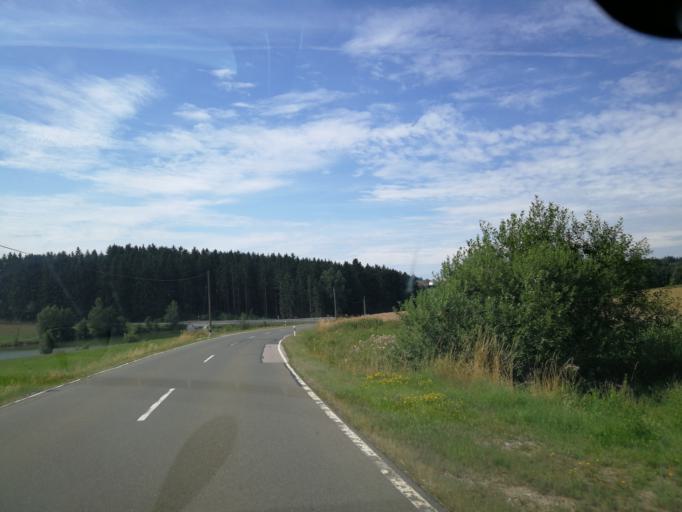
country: DE
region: Bavaria
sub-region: Lower Bavaria
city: Wiesenfelden
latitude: 49.0586
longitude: 12.5199
